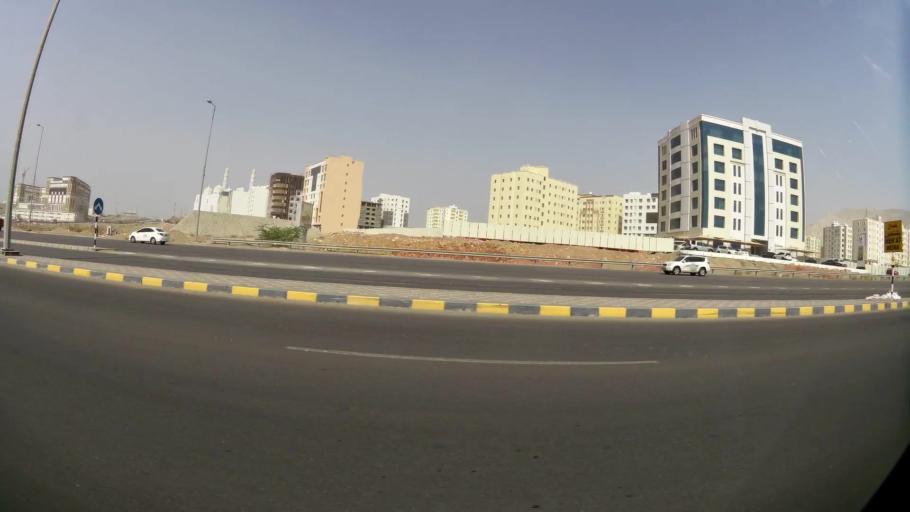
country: OM
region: Muhafazat Masqat
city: Bawshar
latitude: 23.5755
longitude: 58.4078
